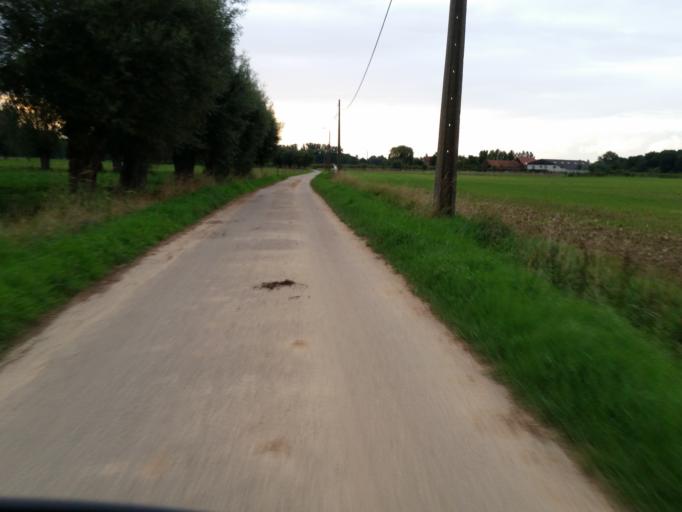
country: BE
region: Flanders
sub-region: Provincie Vlaams-Brabant
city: Zemst
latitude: 50.9910
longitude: 4.4633
